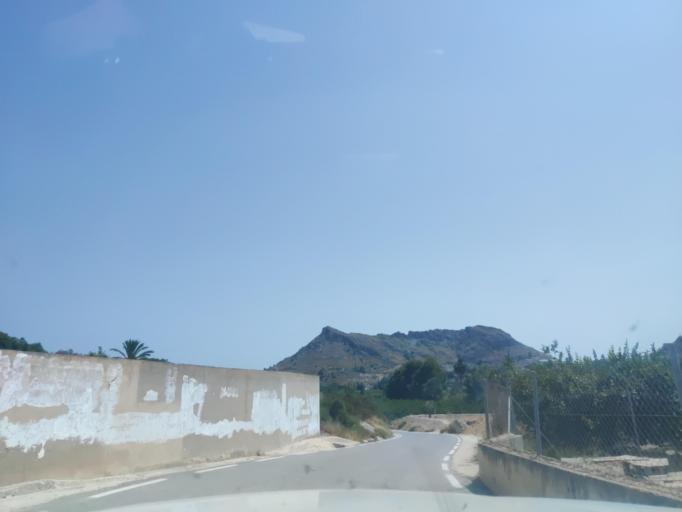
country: ES
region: Murcia
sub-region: Murcia
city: Ulea
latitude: 38.1392
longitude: -1.3184
